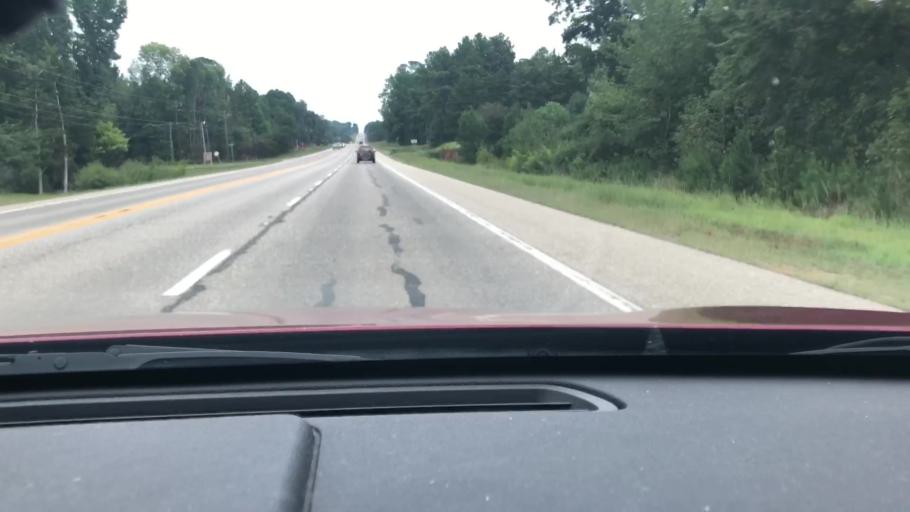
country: US
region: Arkansas
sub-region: Miller County
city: Texarkana
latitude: 33.4296
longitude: -93.9590
